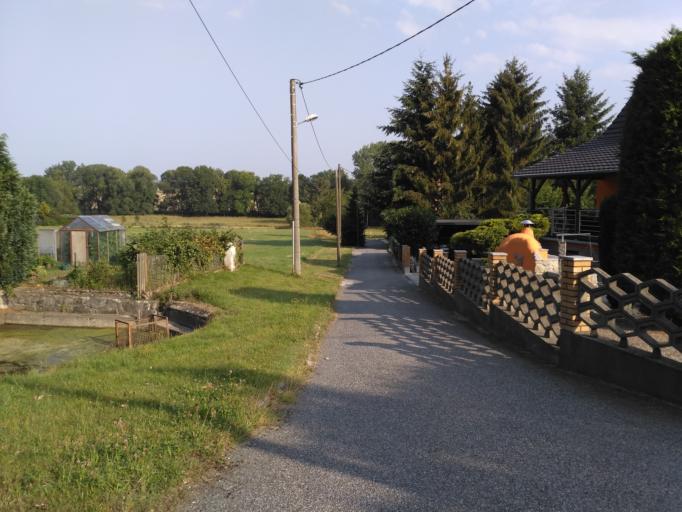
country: DE
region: Saxony
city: Demitz-Thumitz
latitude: 51.1527
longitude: 14.2696
